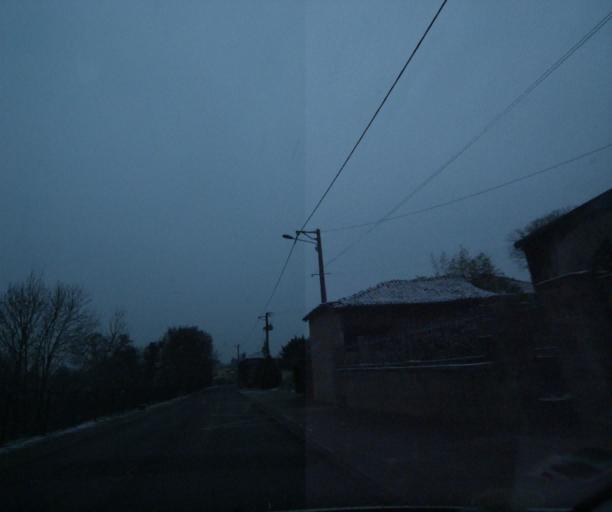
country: FR
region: Champagne-Ardenne
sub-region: Departement de la Haute-Marne
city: Wassy
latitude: 48.4373
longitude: 4.9601
